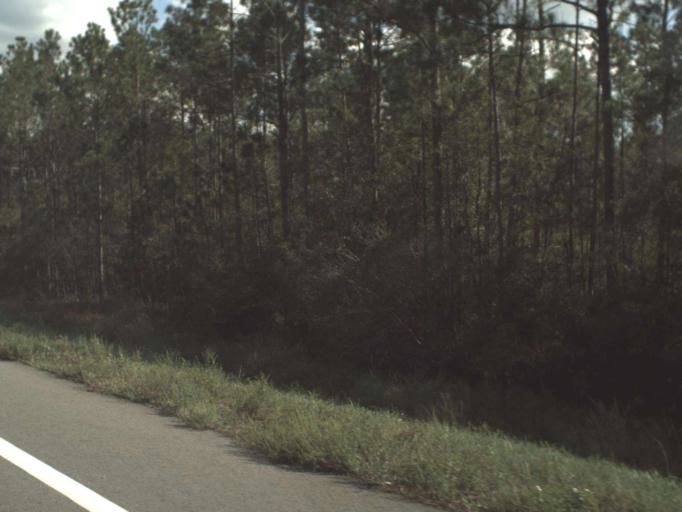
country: US
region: Florida
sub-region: Walton County
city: Freeport
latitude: 30.4585
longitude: -85.9209
